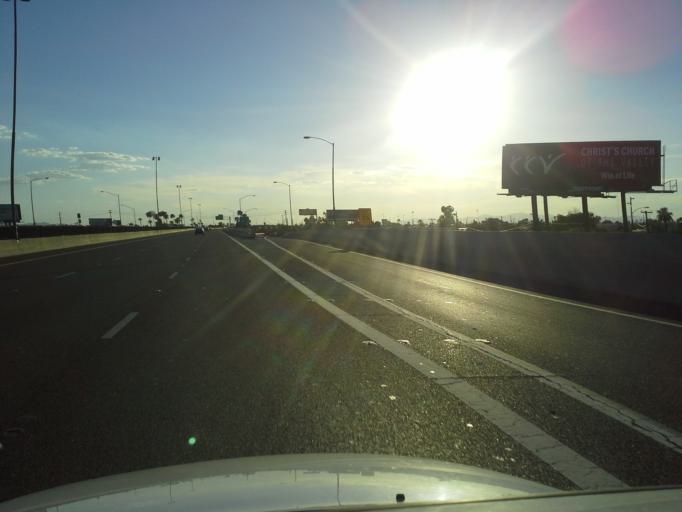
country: US
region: Arizona
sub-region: Maricopa County
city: Phoenix
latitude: 33.4294
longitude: -112.0944
